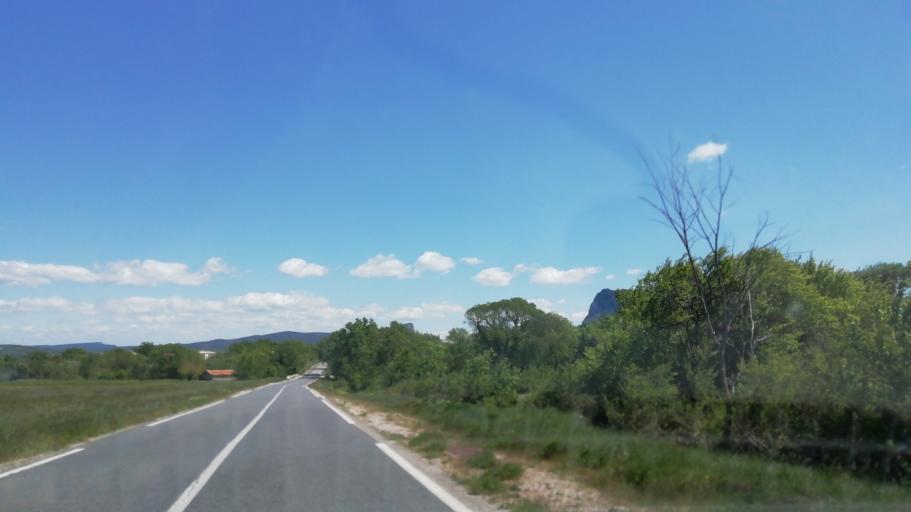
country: FR
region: Languedoc-Roussillon
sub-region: Departement de l'Herault
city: Saint-Martin-de-Londres
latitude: 43.7844
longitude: 3.7507
